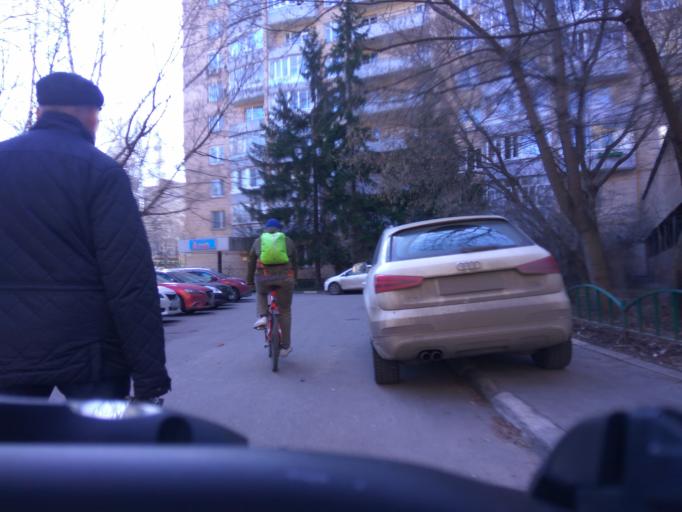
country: RU
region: Moscow
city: Davydkovo
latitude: 55.7341
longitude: 37.4522
